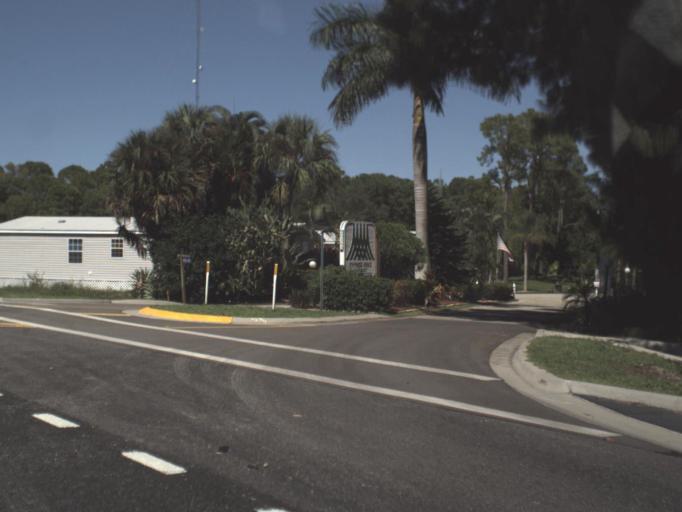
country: US
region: Florida
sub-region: Lee County
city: Estero
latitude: 26.4450
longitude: -81.8130
